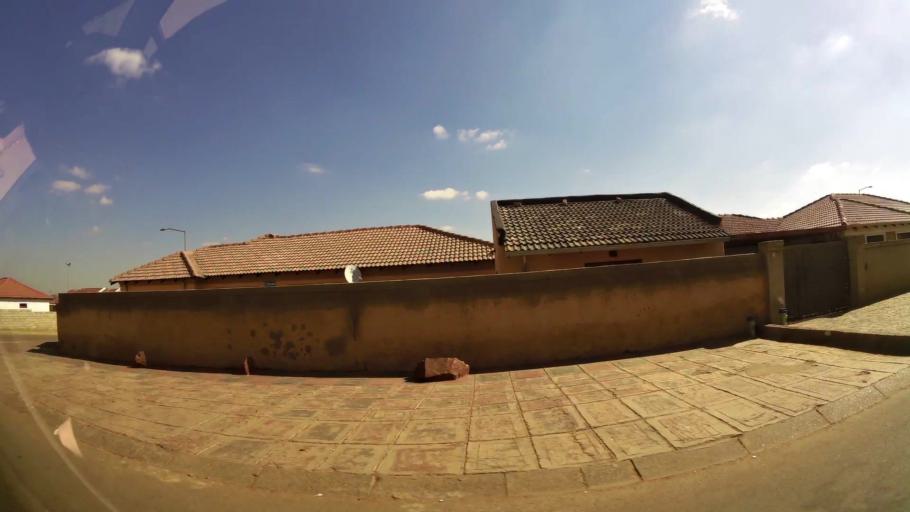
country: ZA
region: Gauteng
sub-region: West Rand District Municipality
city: Krugersdorp
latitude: -26.1490
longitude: 27.7722
